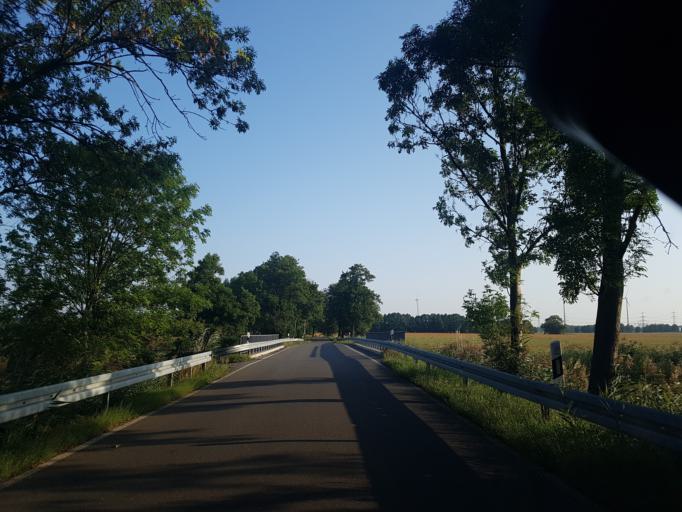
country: DE
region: Saxony-Anhalt
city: Holzdorf
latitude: 51.8169
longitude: 13.1459
